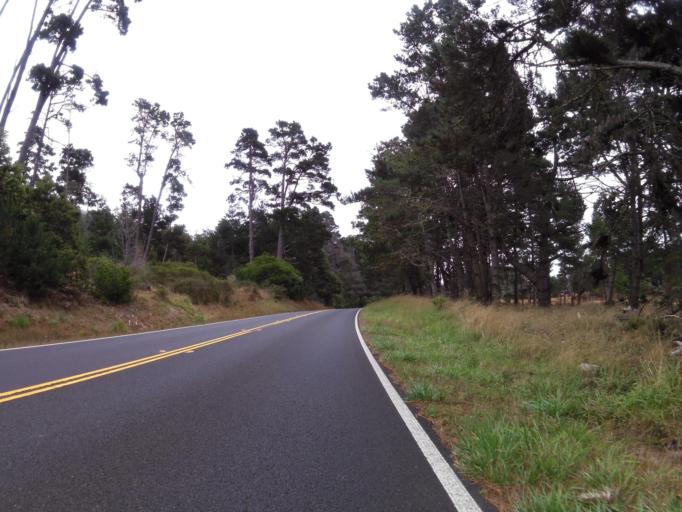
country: US
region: California
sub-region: Sonoma County
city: Sea Ranch
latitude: 38.5398
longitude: -123.2834
